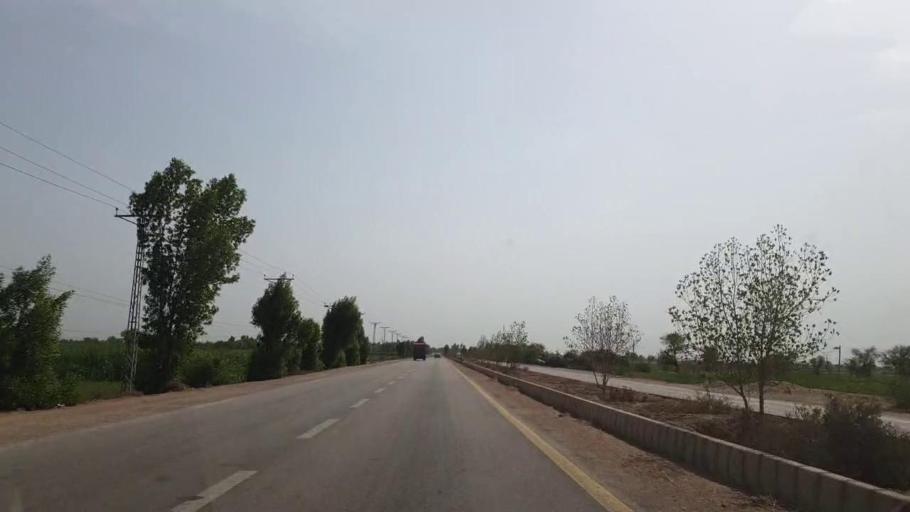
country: PK
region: Sindh
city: Sakrand
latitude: 26.2048
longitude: 68.3175
